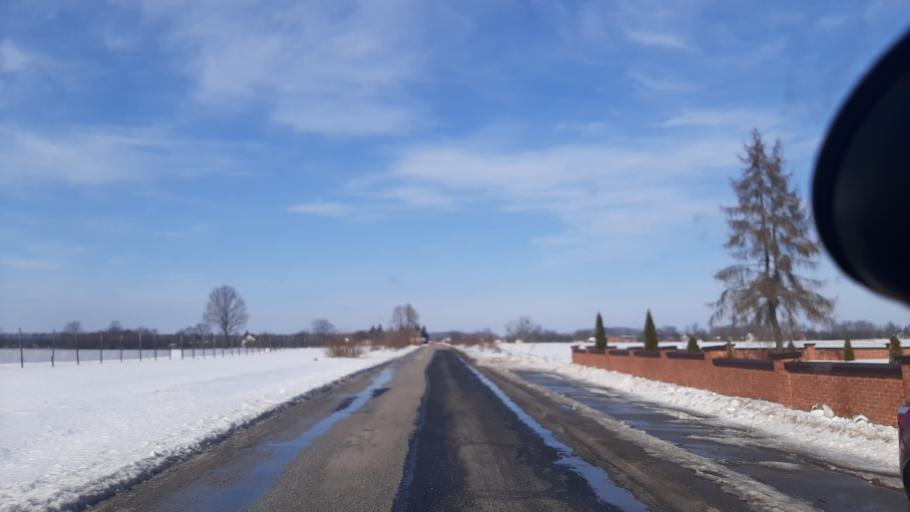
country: PL
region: Lublin Voivodeship
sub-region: Powiat pulawski
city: Kurow
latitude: 51.4479
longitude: 22.1910
